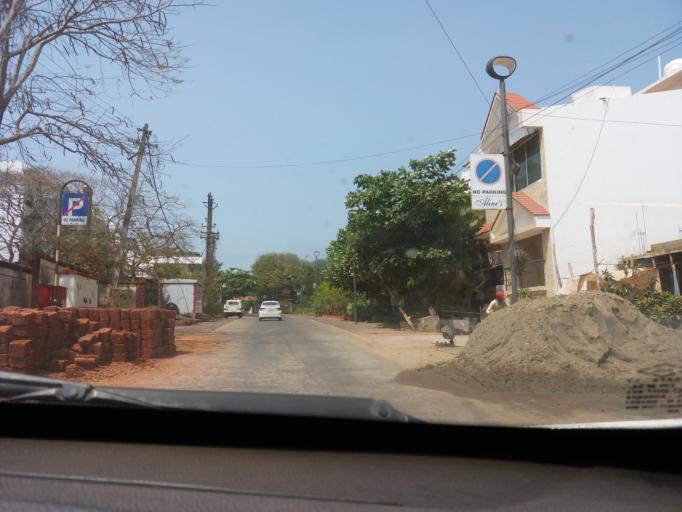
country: IN
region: Goa
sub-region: North Goa
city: Taleigao
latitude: 15.4540
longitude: 73.8028
